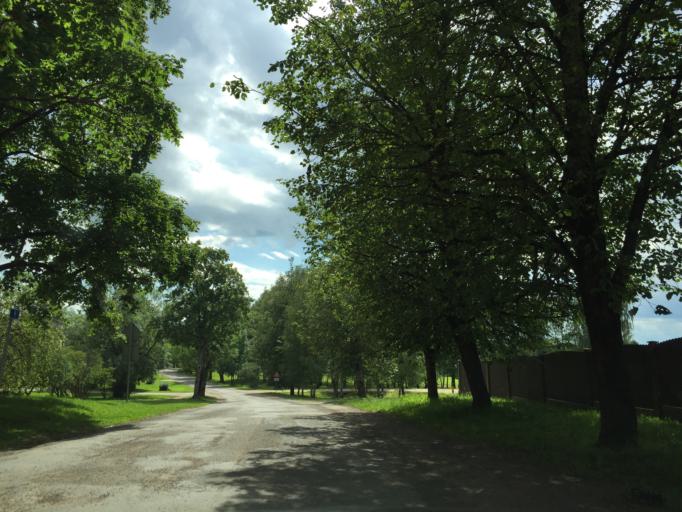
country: LV
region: Malpils
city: Malpils
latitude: 56.8583
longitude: 25.0202
